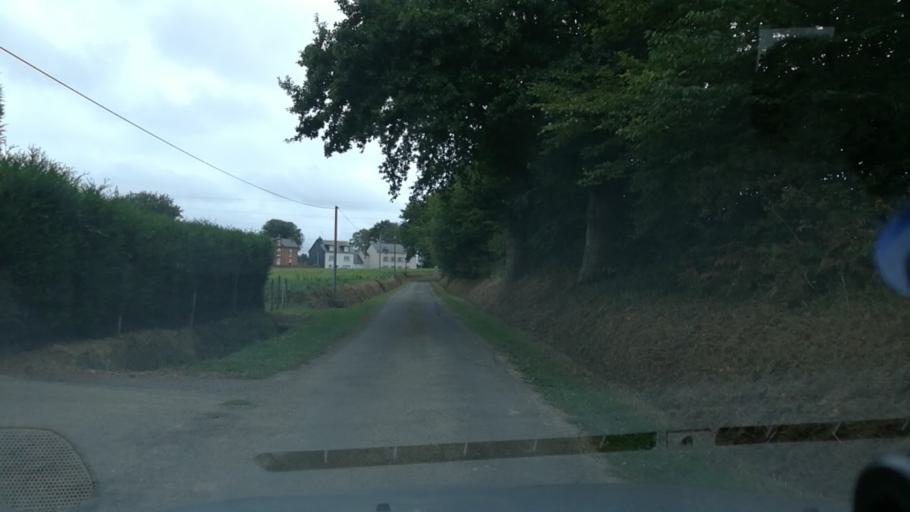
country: FR
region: Brittany
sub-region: Departement d'Ille-et-Vilaine
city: Vezin-le-Coquet
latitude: 48.1159
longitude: -1.7297
